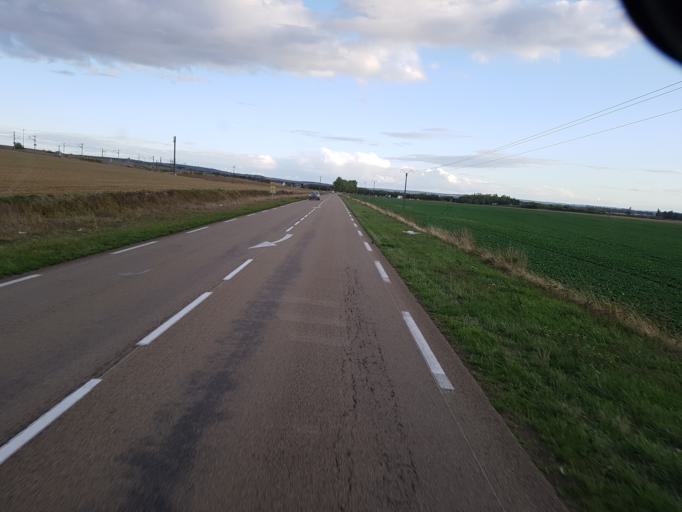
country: FR
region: Bourgogne
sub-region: Departement de l'Yonne
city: Soucy
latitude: 48.2665
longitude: 3.2788
